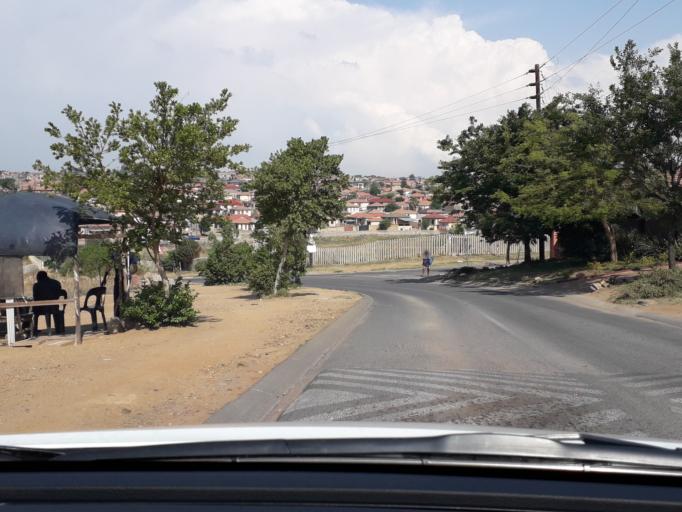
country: ZA
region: Gauteng
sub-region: West Rand District Municipality
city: Muldersdriseloop
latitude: -26.0412
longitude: 27.9146
